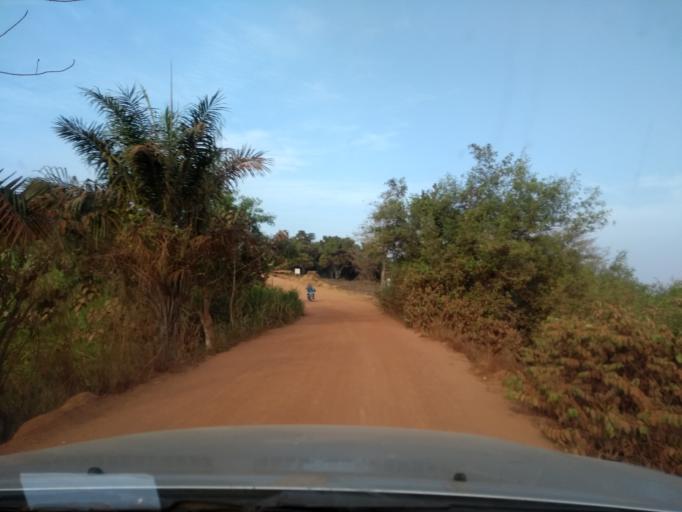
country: GN
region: Kindia
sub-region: Prefecture de Dubreka
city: Dubreka
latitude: 9.7889
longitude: -13.5330
